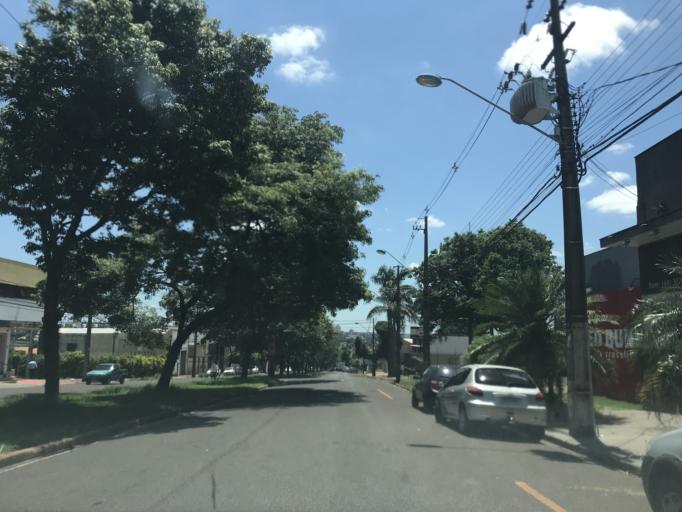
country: BR
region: Parana
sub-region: Maringa
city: Maringa
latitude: -23.4487
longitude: -51.9478
